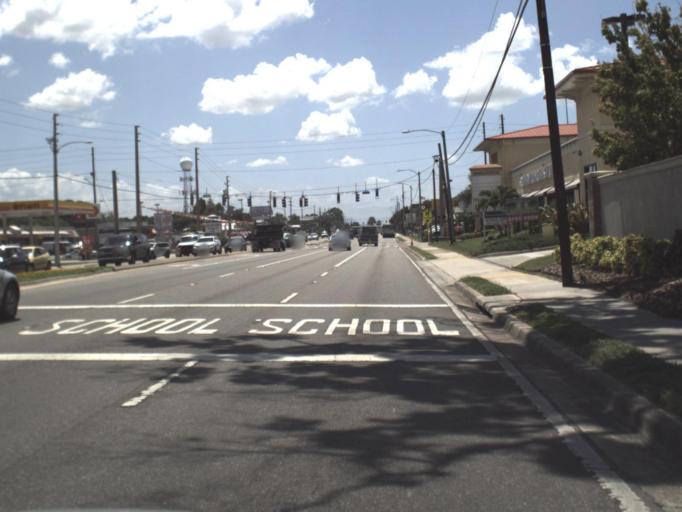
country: US
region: Florida
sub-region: Pinellas County
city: Pinellas Park
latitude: 27.8475
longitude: -82.7288
